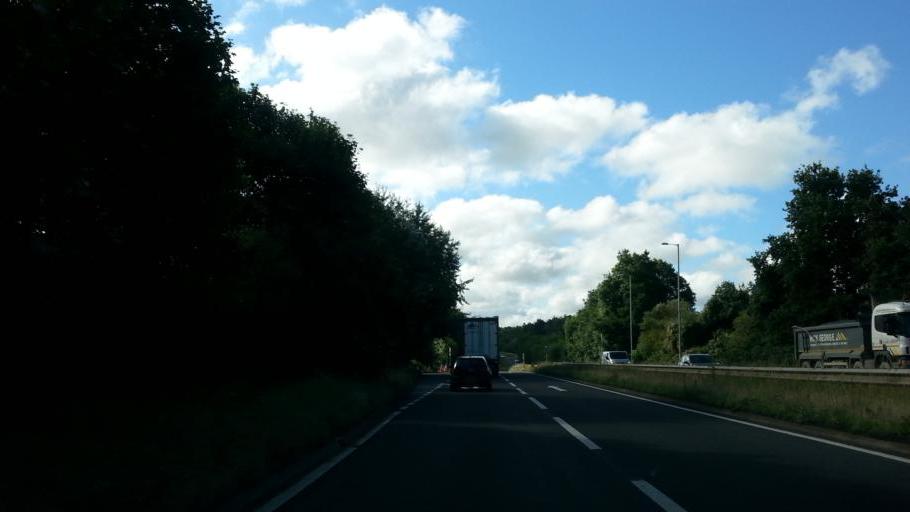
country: GB
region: England
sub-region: Northamptonshire
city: Northampton
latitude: 52.2624
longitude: -0.8415
